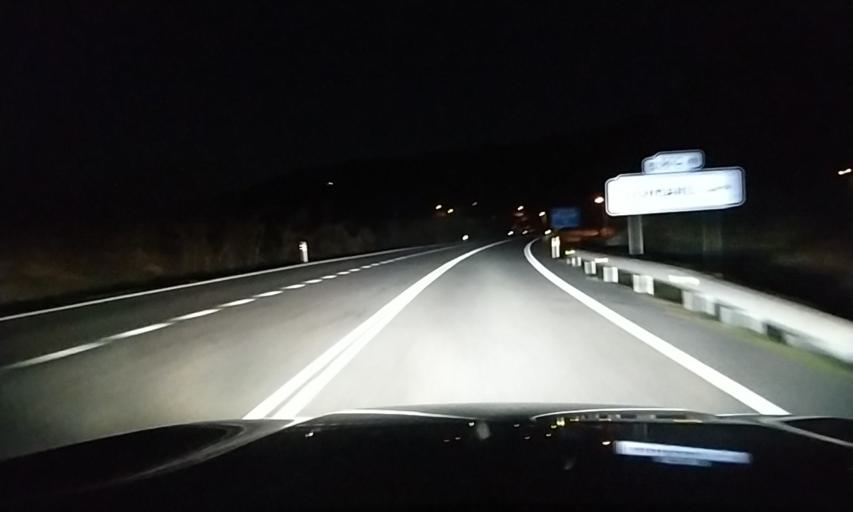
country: ES
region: Galicia
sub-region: Provincia de Ourense
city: Cualedro
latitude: 41.9732
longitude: -7.5198
